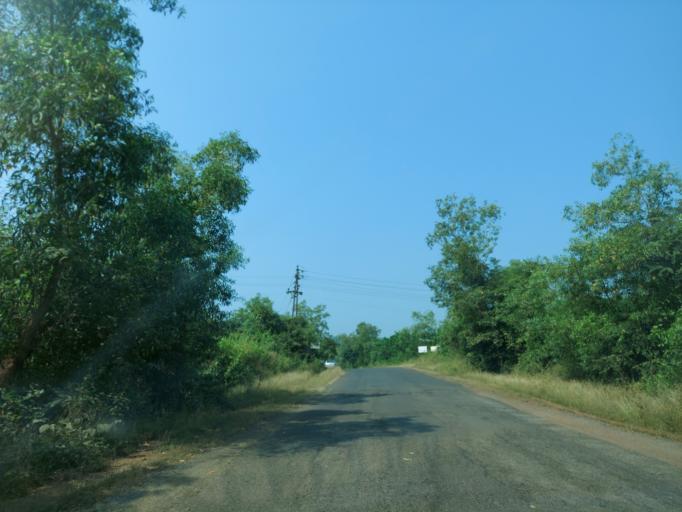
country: IN
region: Maharashtra
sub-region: Sindhudurg
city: Kudal
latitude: 15.9771
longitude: 73.6163
